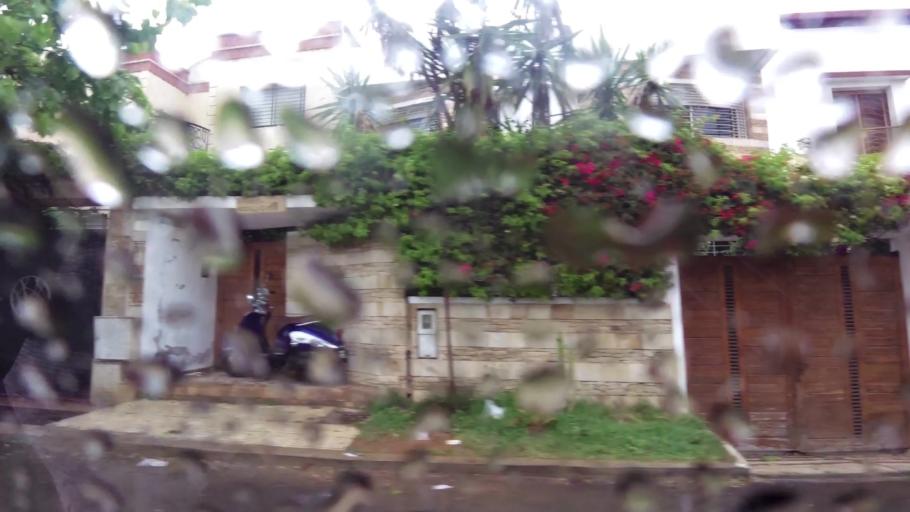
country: MA
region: Grand Casablanca
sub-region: Casablanca
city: Casablanca
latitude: 33.5447
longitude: -7.6677
